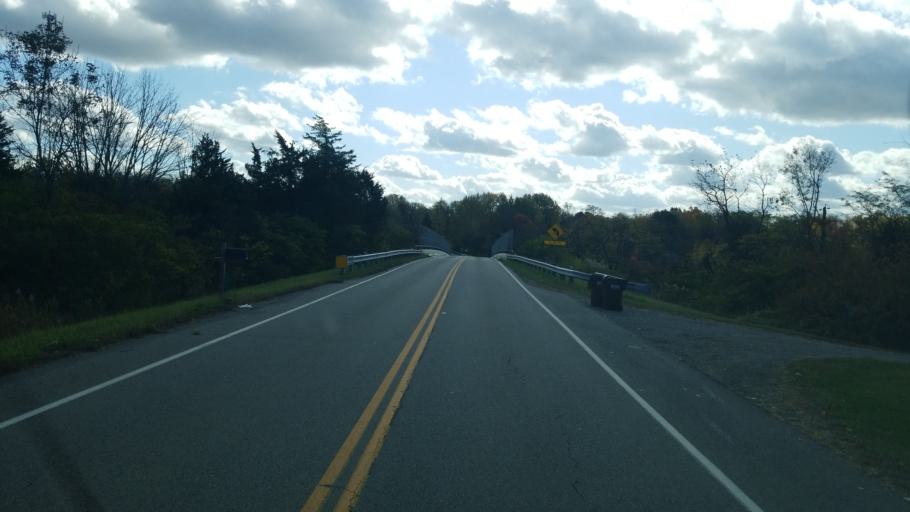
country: US
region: Ohio
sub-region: Warren County
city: Lebanon
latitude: 39.4037
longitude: -84.1790
